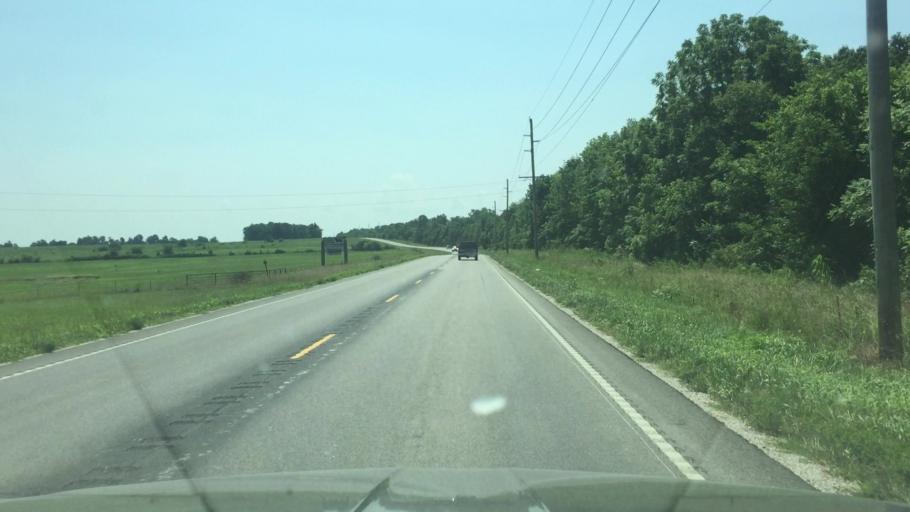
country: US
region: Missouri
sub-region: Miller County
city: Eldon
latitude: 38.3912
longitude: -92.7075
